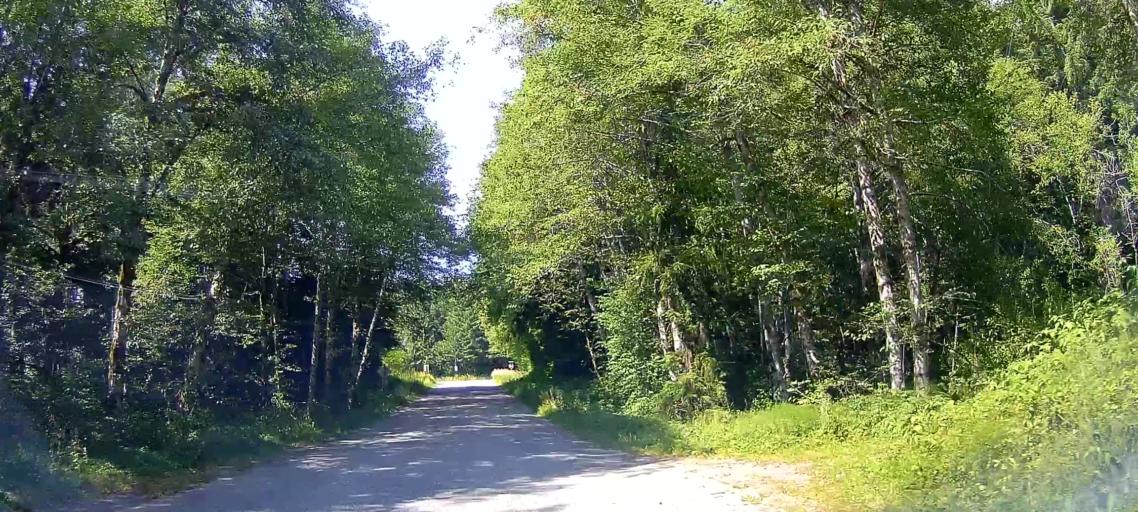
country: US
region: Washington
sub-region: Snohomish County
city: Arlington Heights
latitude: 48.3347
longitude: -122.0347
